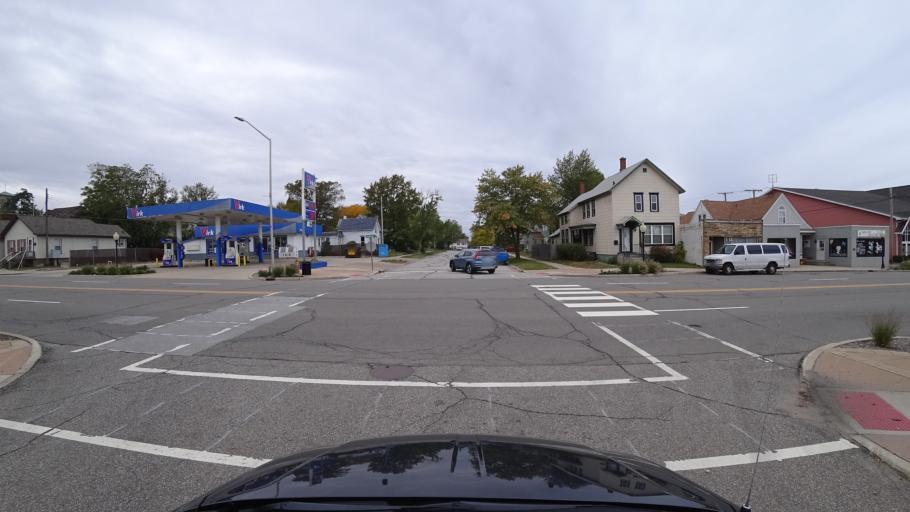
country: US
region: Indiana
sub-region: LaPorte County
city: Michigan City
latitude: 41.7100
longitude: -86.8980
